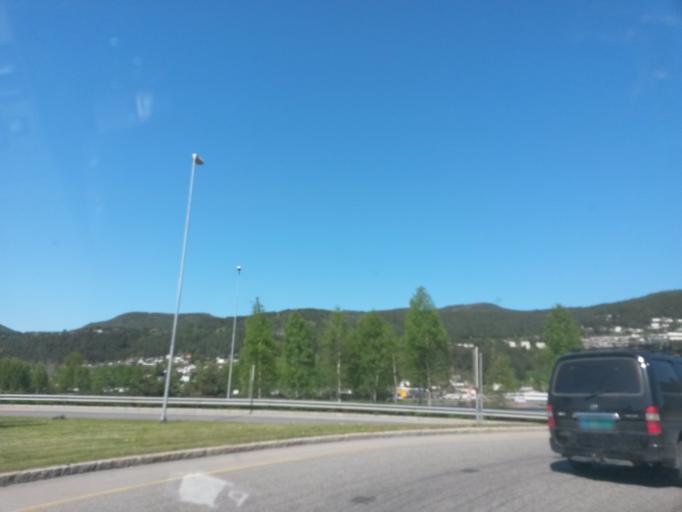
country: NO
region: Buskerud
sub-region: Nedre Eiker
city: Mjondalen
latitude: 59.7518
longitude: 10.0257
